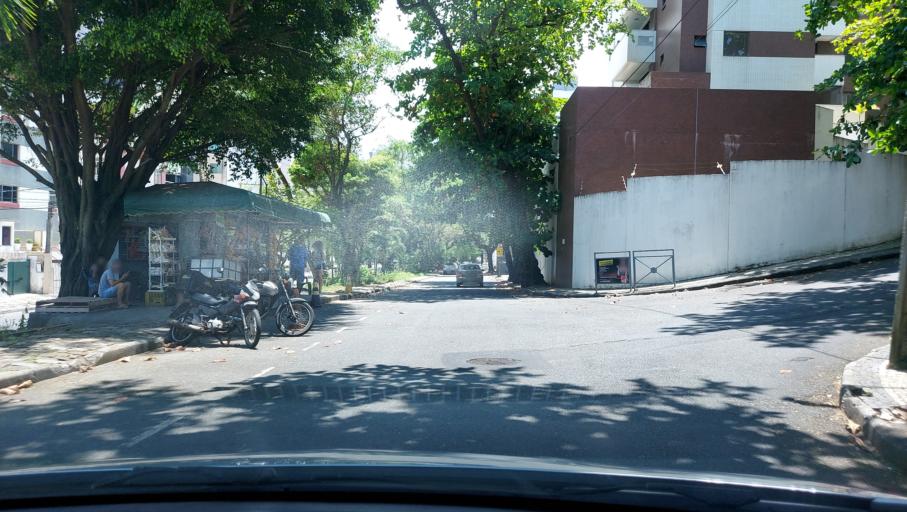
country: BR
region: Bahia
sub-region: Salvador
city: Salvador
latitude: -12.9942
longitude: -38.4529
